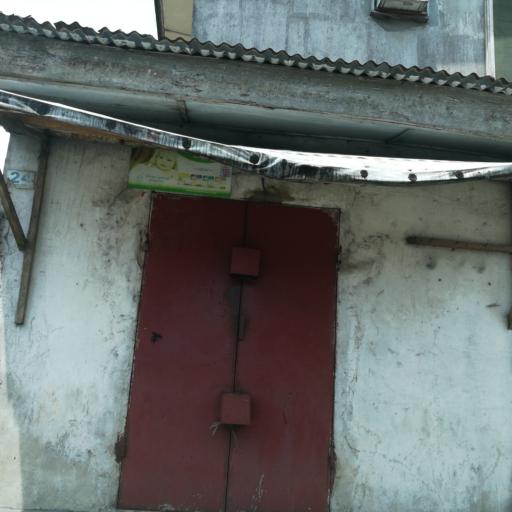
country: NG
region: Rivers
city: Port Harcourt
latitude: 4.7813
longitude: 7.0361
